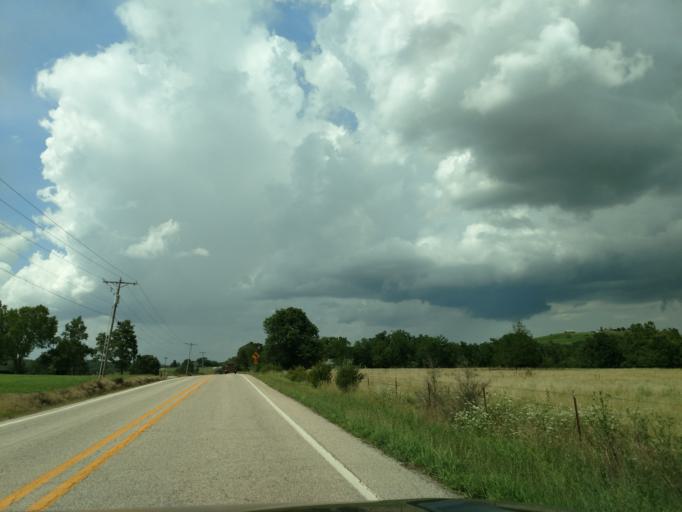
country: US
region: Arkansas
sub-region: Boone County
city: Harrison
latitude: 36.2681
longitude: -93.2320
